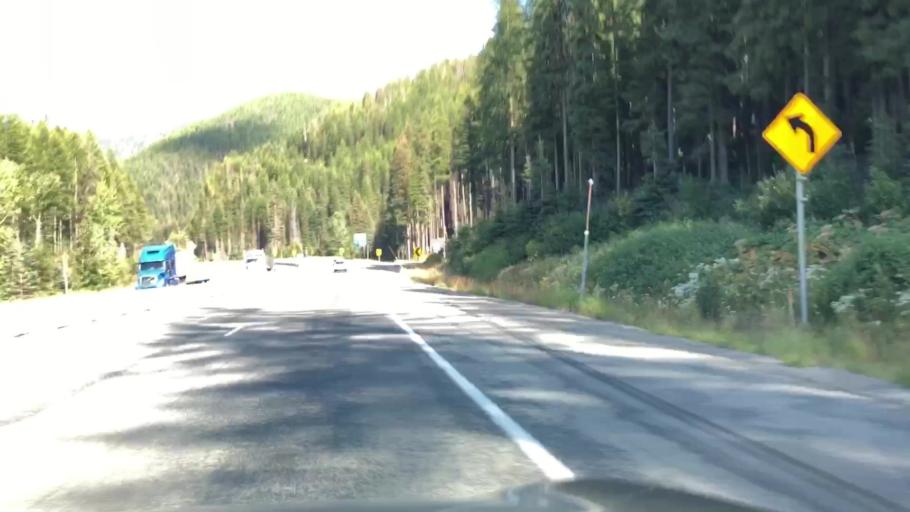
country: US
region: Idaho
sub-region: Shoshone County
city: Wallace
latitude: 47.4337
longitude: -115.6667
